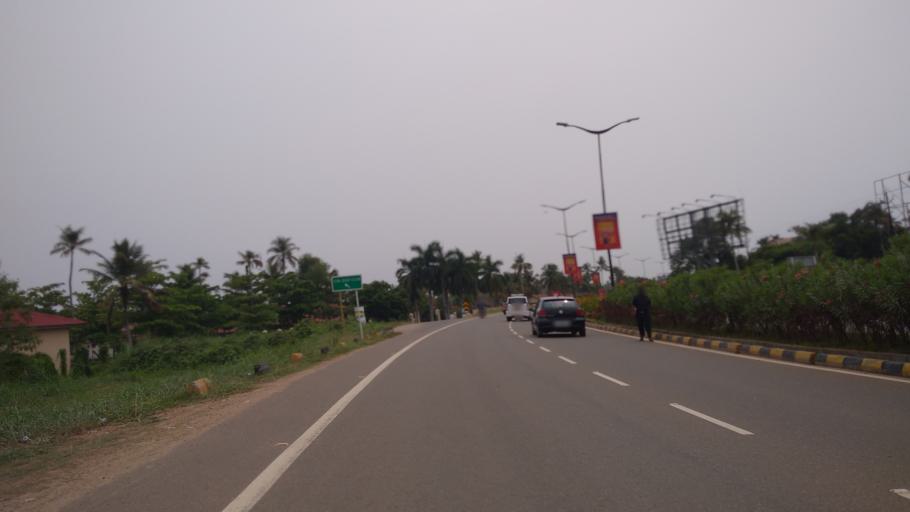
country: IN
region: Kerala
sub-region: Ernakulam
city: Angamali
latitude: 10.1540
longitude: 76.3756
